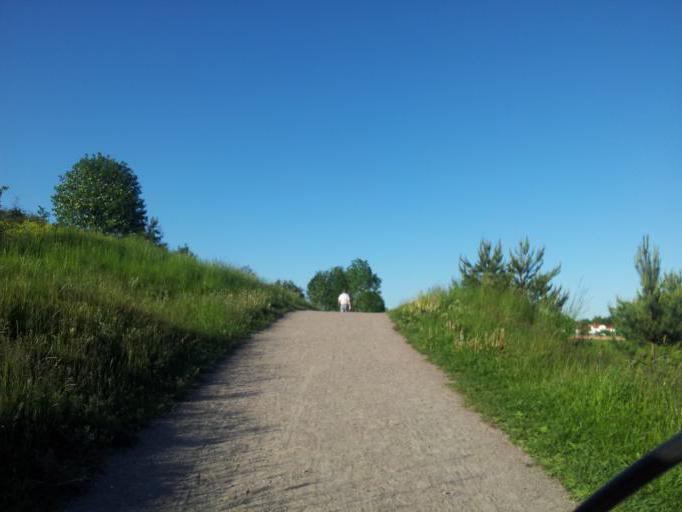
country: SE
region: Uppsala
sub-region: Uppsala Kommun
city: Gamla Uppsala
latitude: 59.8937
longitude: 17.6254
